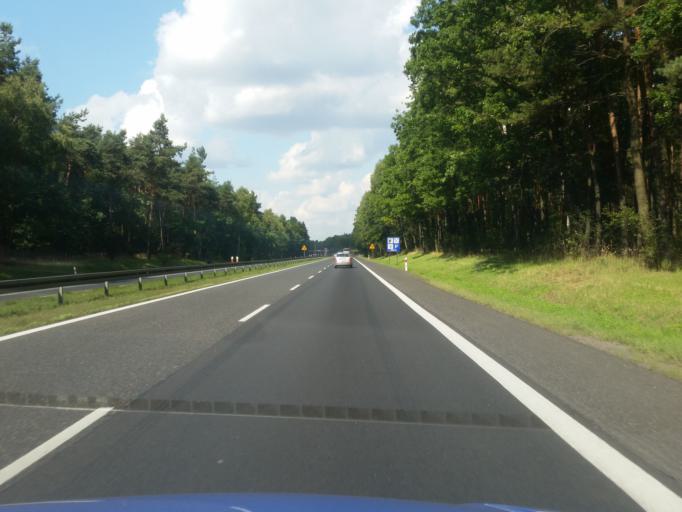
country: PL
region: Silesian Voivodeship
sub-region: Powiat czestochowski
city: Kamienica Polska
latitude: 50.6553
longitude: 19.1316
